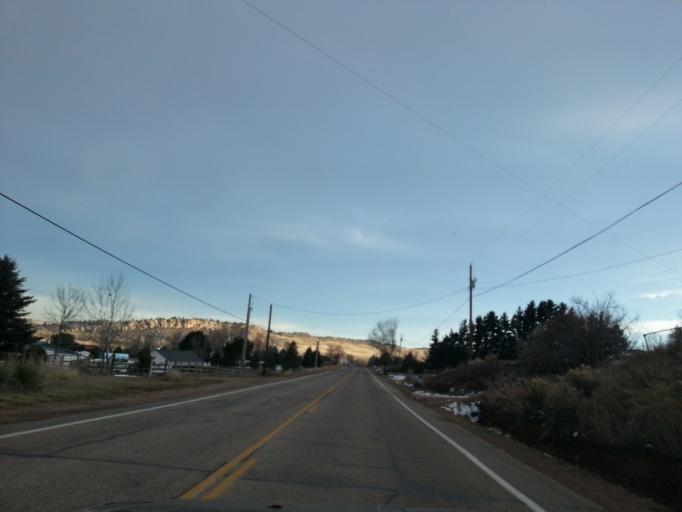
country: US
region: Colorado
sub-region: Larimer County
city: Loveland
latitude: 40.4253
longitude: -105.1928
